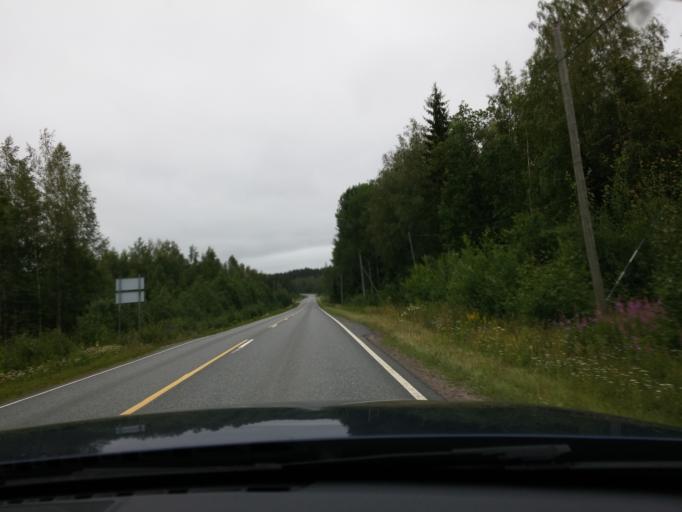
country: FI
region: Central Finland
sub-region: Joutsa
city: Joutsa
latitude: 61.7853
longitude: 26.0456
